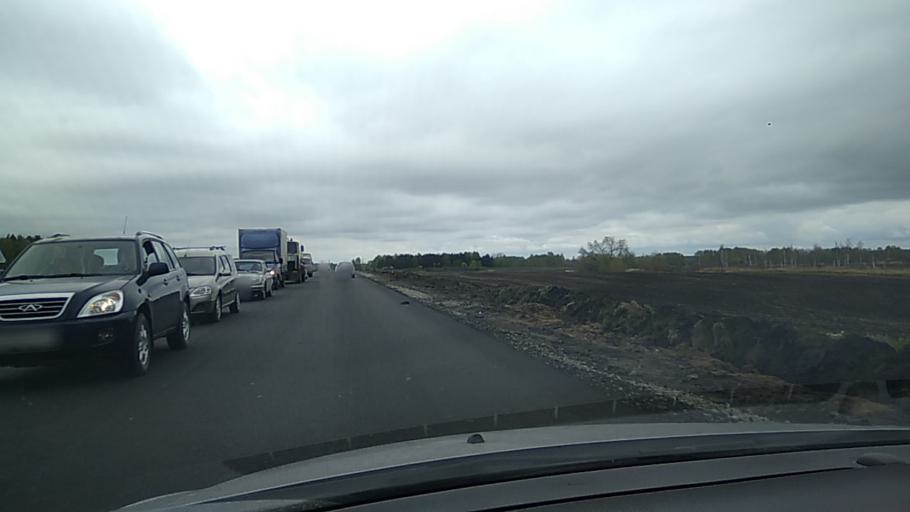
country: RU
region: Kurgan
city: Shadrinsk
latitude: 56.1543
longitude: 63.4043
